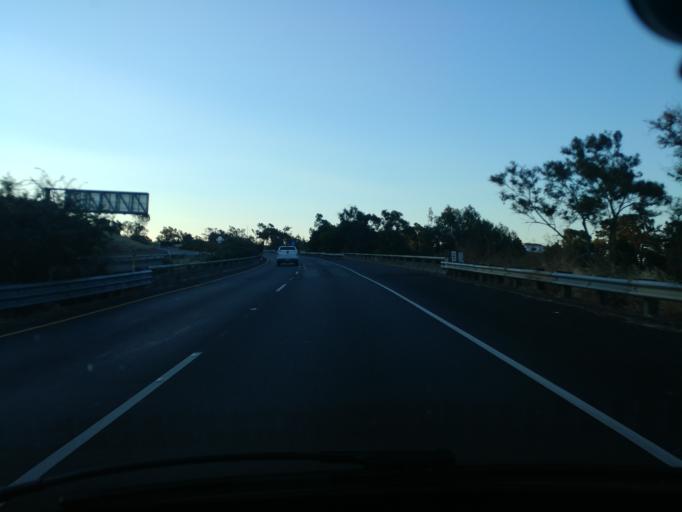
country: US
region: California
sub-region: Solano County
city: Benicia
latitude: 38.0691
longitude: -122.1834
